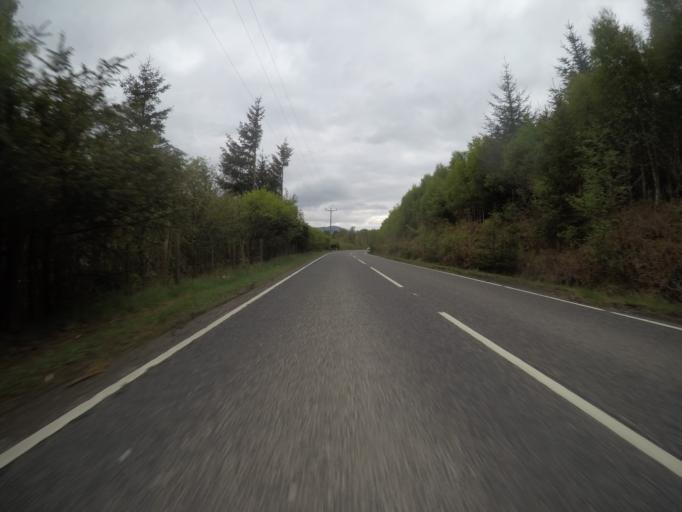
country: GB
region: Scotland
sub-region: Highland
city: Beauly
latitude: 57.1959
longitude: -4.6127
